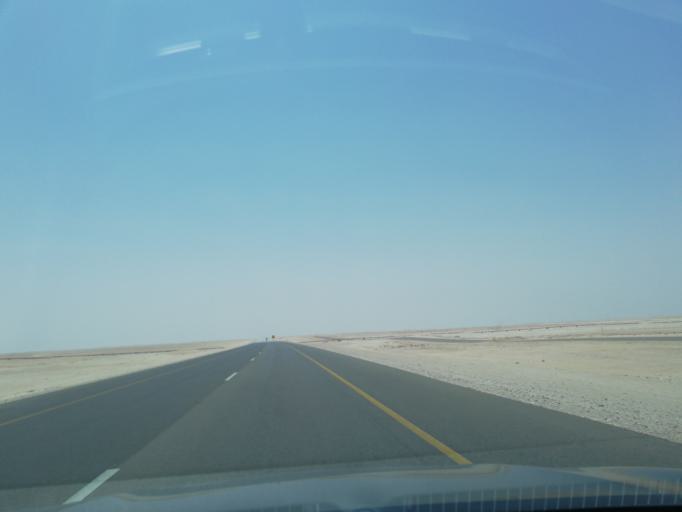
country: OM
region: Al Wusta
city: Hayma'
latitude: 19.7091
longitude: 55.9950
